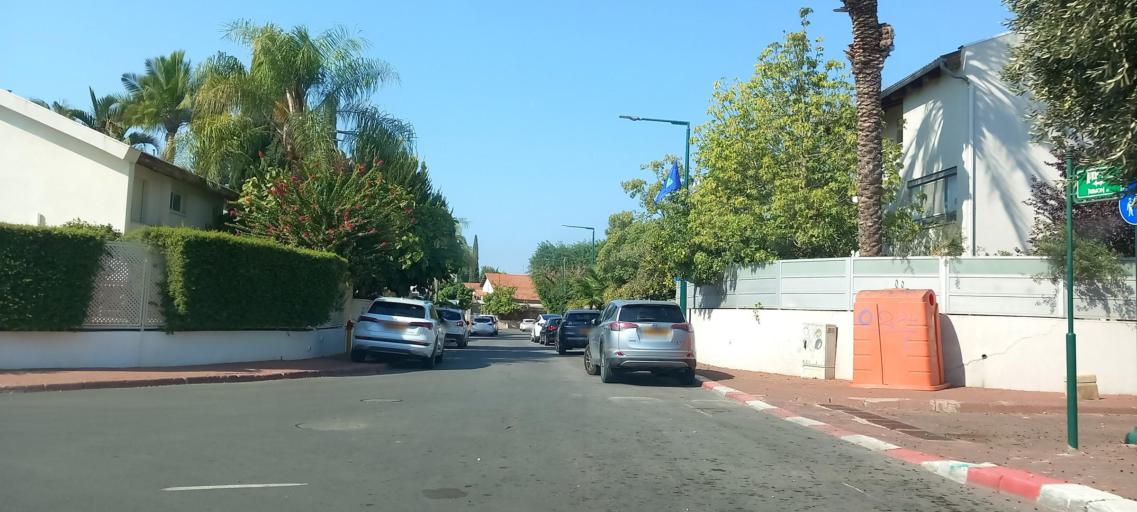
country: IL
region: Tel Aviv
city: Or Yehuda
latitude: 32.0436
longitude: 34.8366
